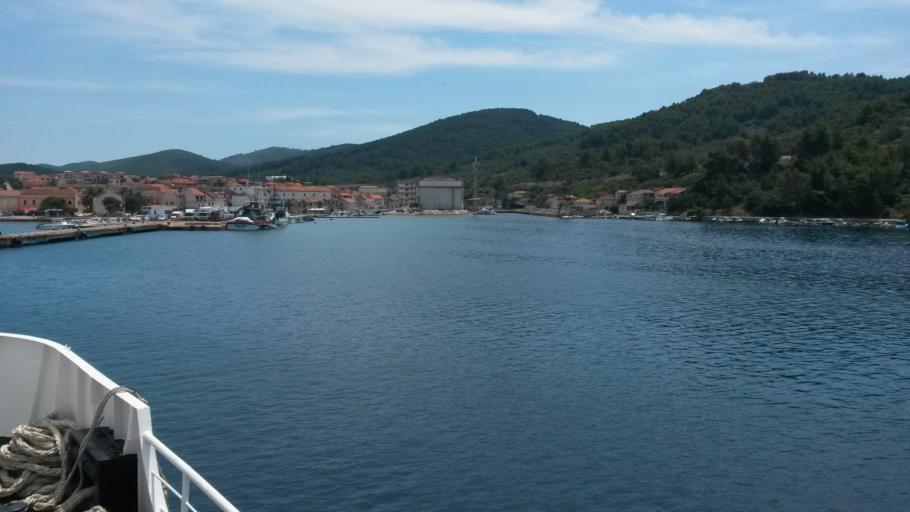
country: HR
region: Dubrovacko-Neretvanska
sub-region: Grad Dubrovnik
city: Vela Luka
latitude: 42.9605
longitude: 16.7086
